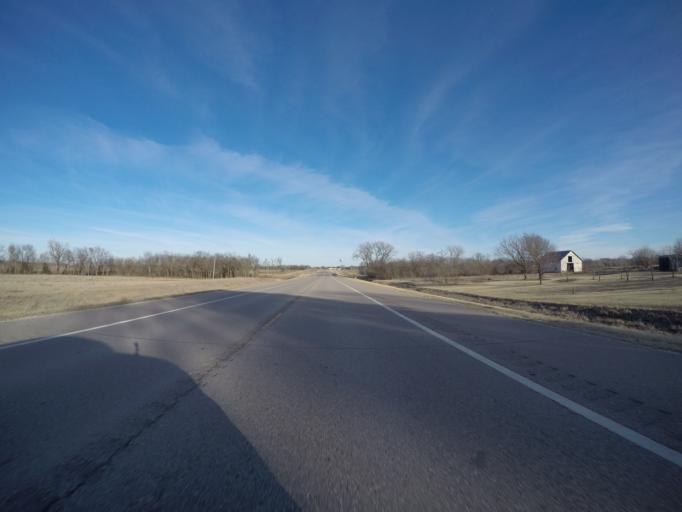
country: US
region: Kansas
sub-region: Marion County
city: Peabody
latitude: 38.1745
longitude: -97.1292
